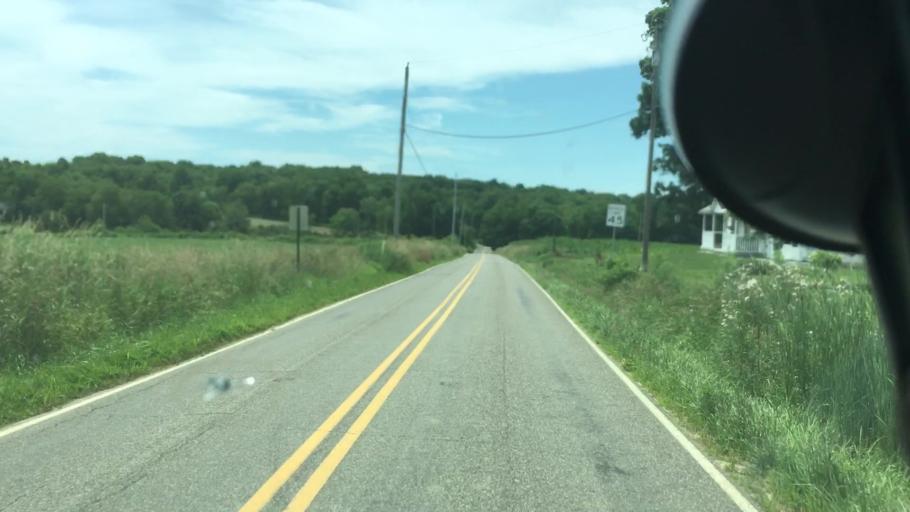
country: US
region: Pennsylvania
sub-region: Mercer County
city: Mercer
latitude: 41.2271
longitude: -80.1999
